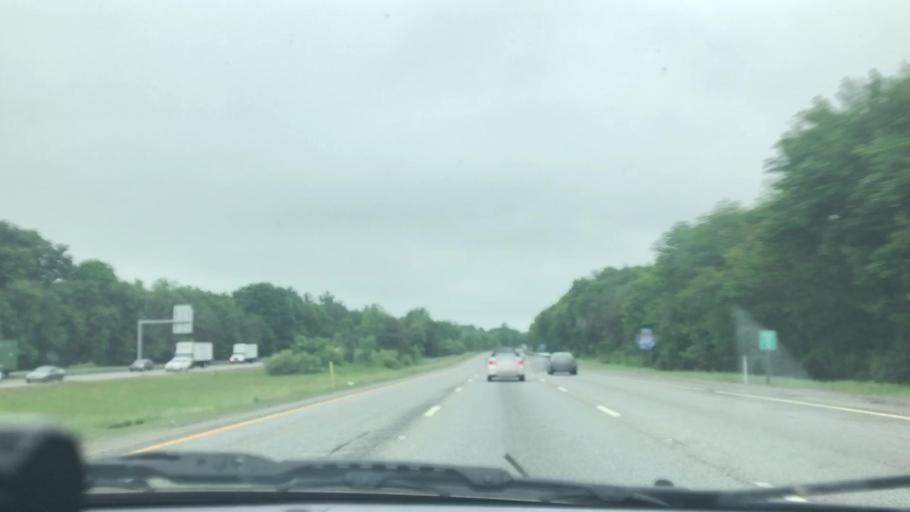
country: US
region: Massachusetts
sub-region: Worcester County
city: Bolton
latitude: 42.4359
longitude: -71.5901
